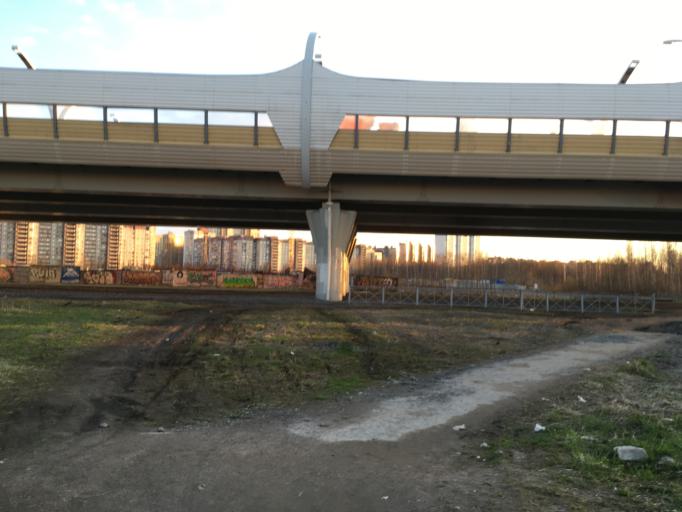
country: RU
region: Leningrad
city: Untolovo
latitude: 60.0115
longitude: 30.2326
